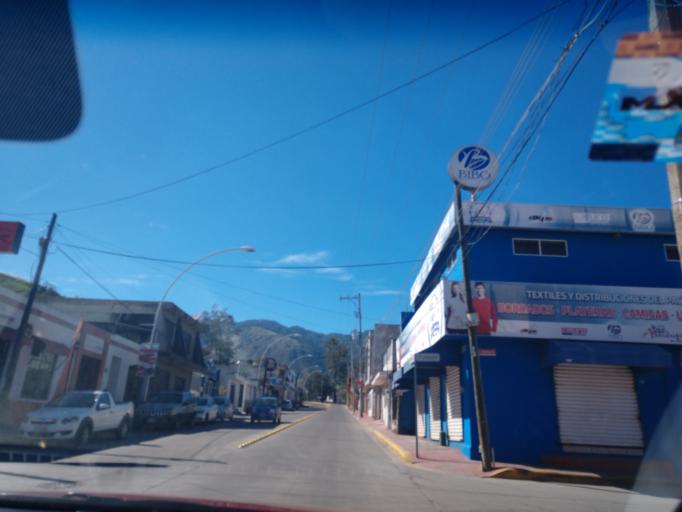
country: MX
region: Nayarit
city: Tepic
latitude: 21.4845
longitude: -104.8995
